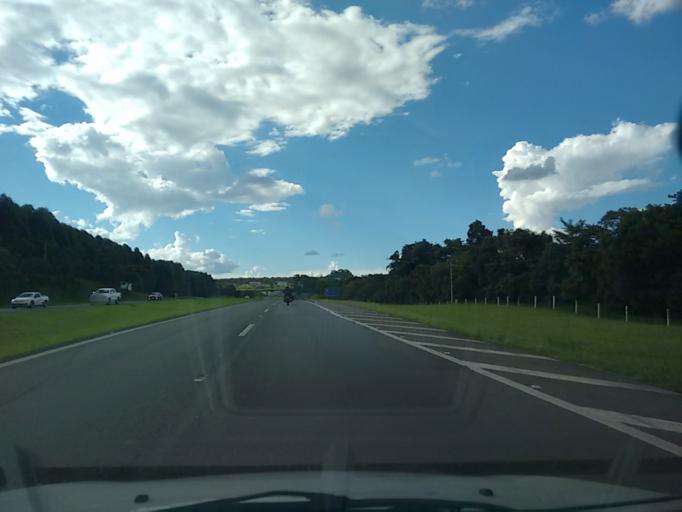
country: BR
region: Sao Paulo
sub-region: Sao Carlos
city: Sao Carlos
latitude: -22.0511
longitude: -47.8578
